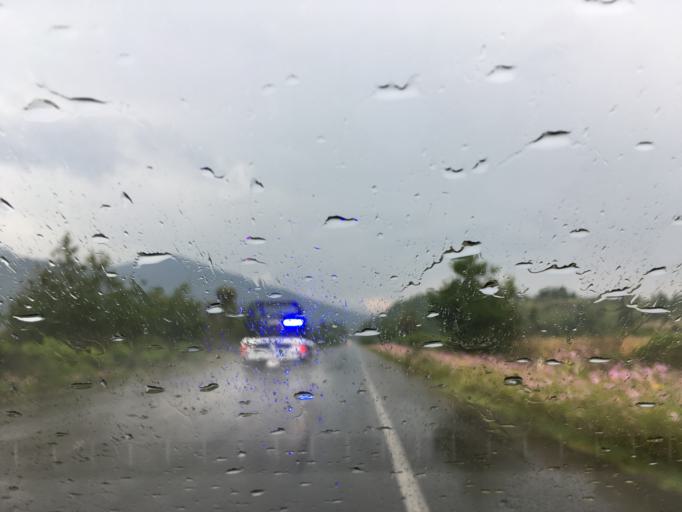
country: MX
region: Michoacan
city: Angahuan
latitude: 19.5652
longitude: -102.2399
